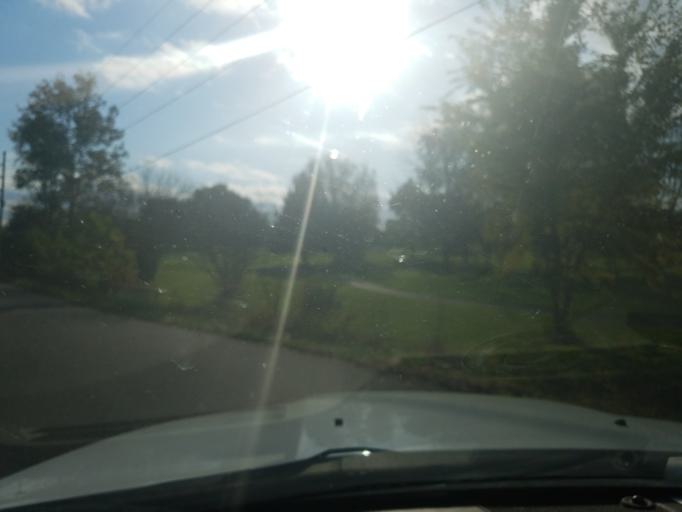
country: US
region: Indiana
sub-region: Jackson County
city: Seymour
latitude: 38.9654
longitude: -85.8532
